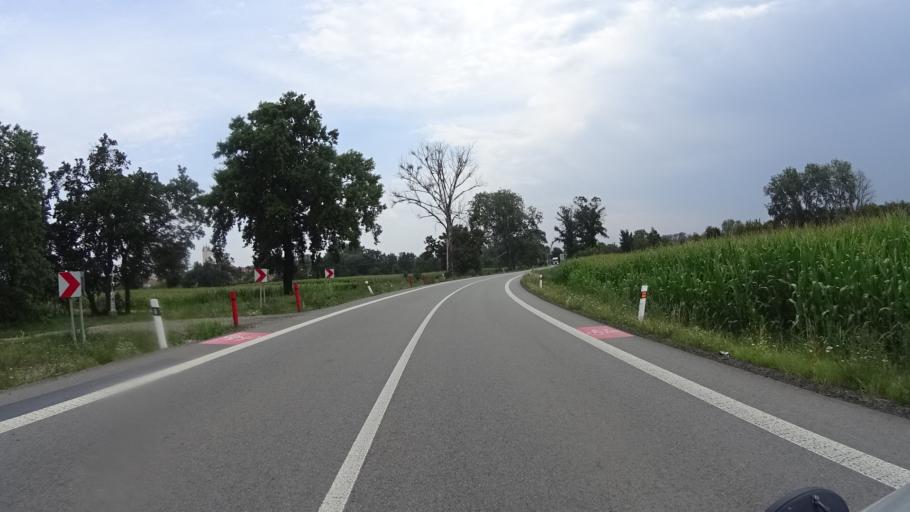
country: CZ
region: South Moravian
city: Podivin
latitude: 48.8210
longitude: 16.8401
